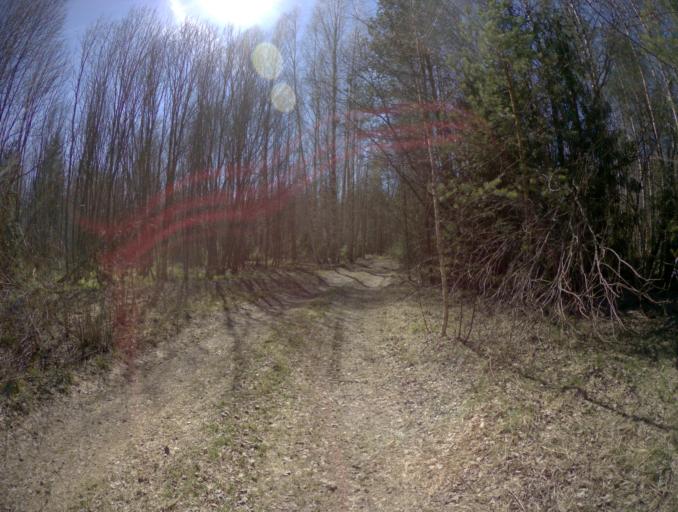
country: RU
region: Vladimir
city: Ivanishchi
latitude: 55.8313
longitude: 40.4300
